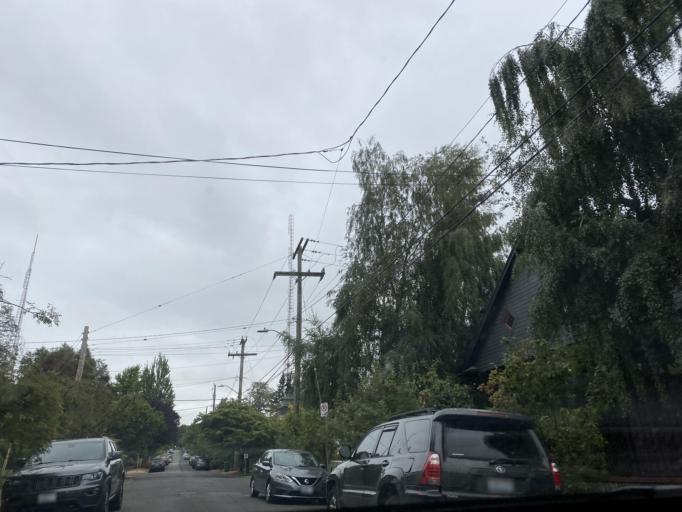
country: US
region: Washington
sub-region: King County
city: Seattle
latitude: 47.6364
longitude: -122.3557
